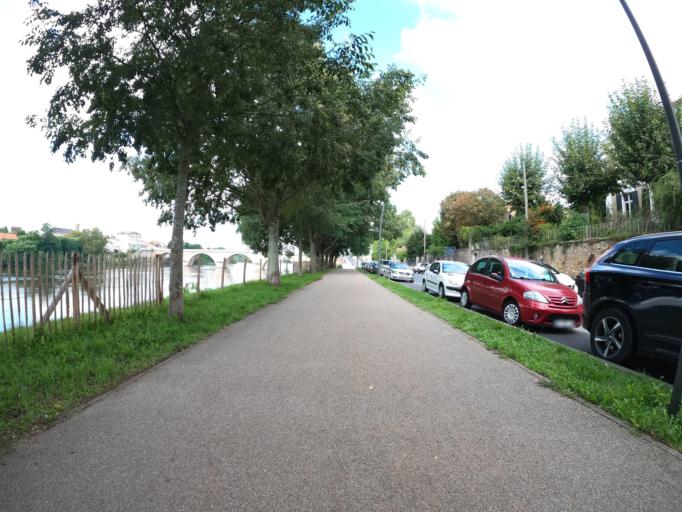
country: FR
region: Aquitaine
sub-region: Departement de la Dordogne
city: Bergerac
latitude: 44.8472
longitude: 0.4862
